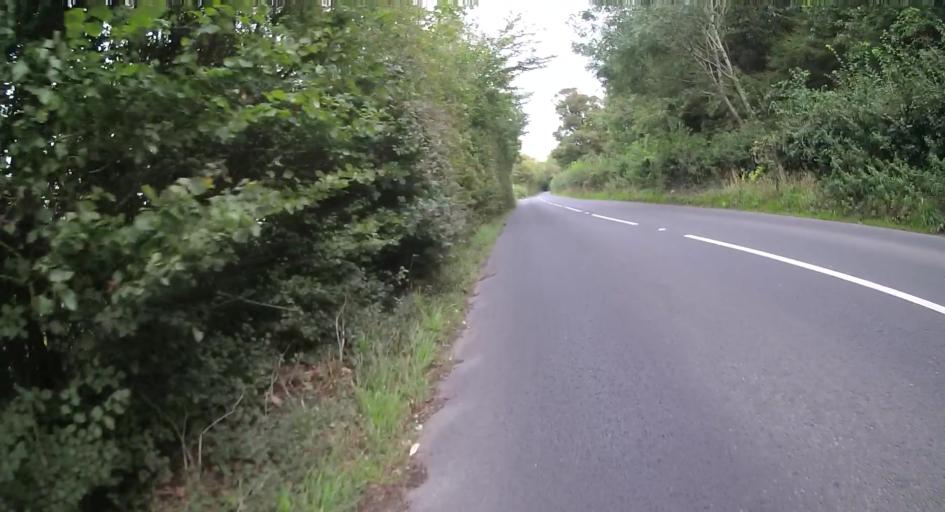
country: GB
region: England
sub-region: Isle of Wight
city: Shalfleet
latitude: 50.6853
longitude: -1.3779
